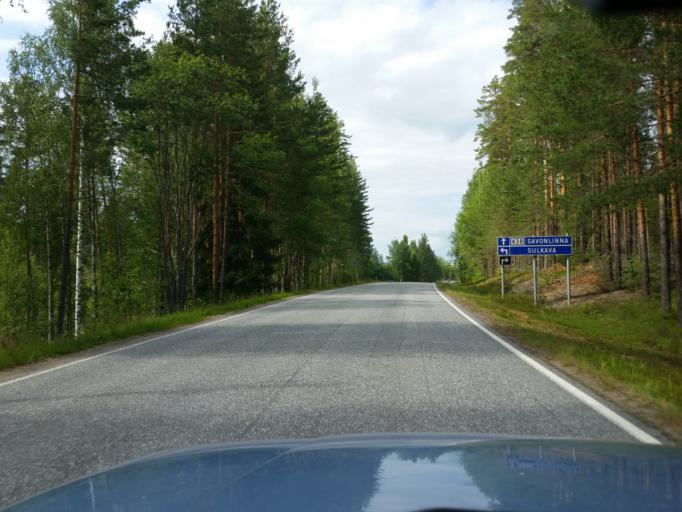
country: FI
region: Southern Savonia
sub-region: Savonlinna
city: Sulkava
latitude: 61.7977
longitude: 28.4156
